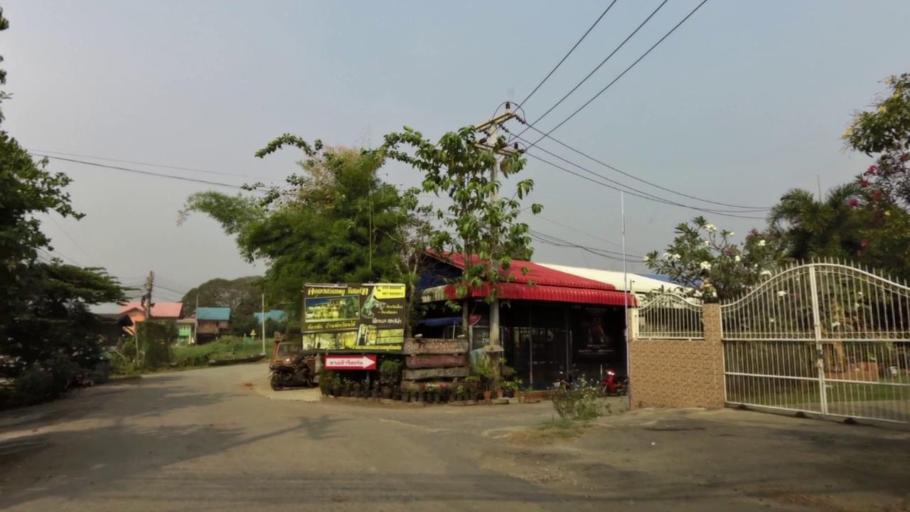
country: TH
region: Phra Nakhon Si Ayutthaya
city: Phra Nakhon Si Ayutthaya
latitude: 14.3359
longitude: 100.5786
